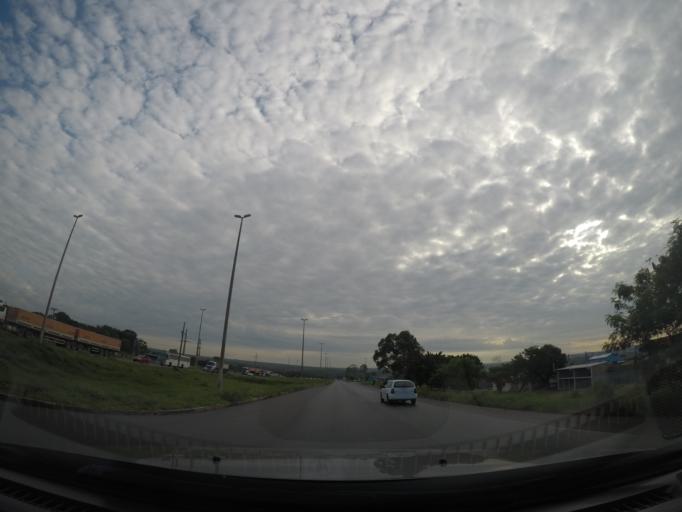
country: BR
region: Goias
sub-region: Planaltina
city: Planaltina
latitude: -15.5993
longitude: -47.6772
